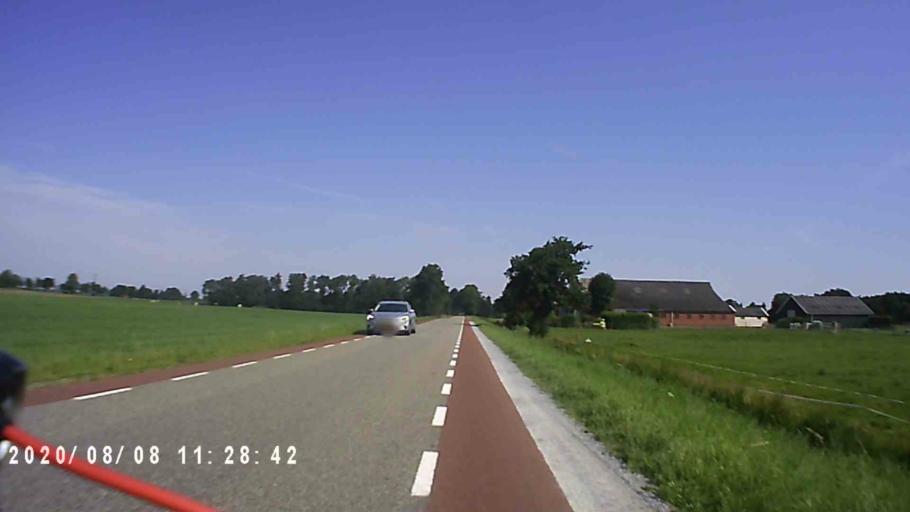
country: NL
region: Groningen
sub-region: Gemeente Leek
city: Leek
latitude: 53.1932
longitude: 6.3863
